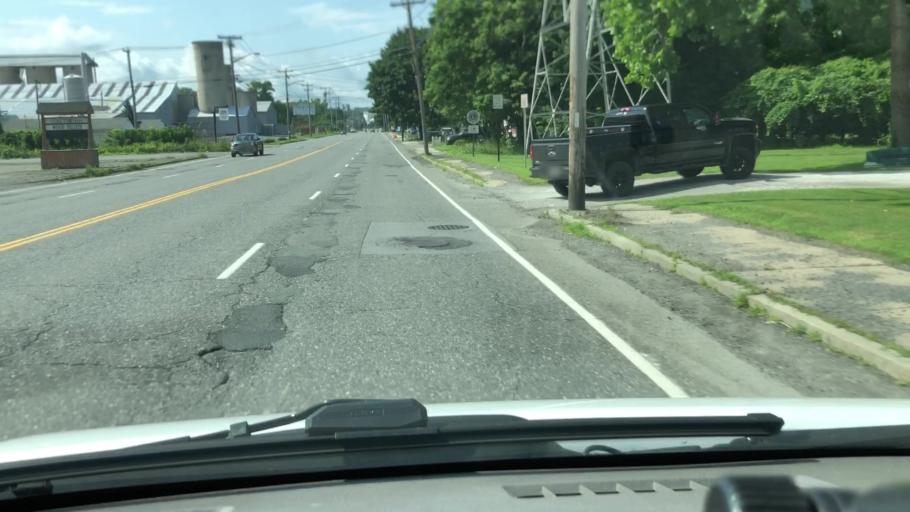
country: US
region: Massachusetts
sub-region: Berkshire County
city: Adams
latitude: 42.6554
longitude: -73.1100
